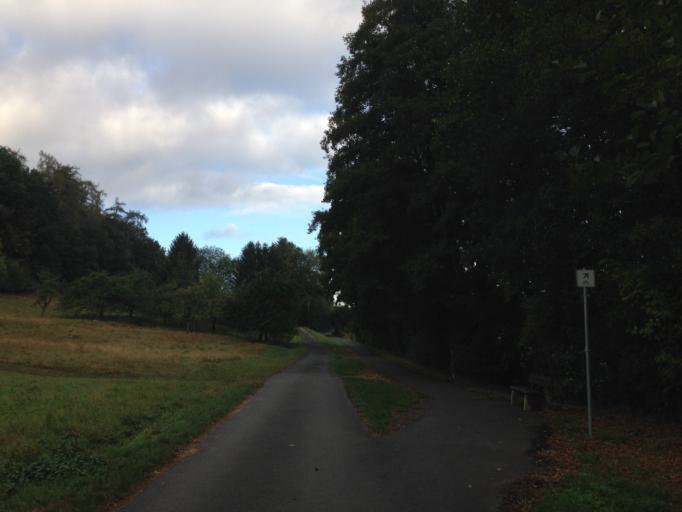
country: DE
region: Hesse
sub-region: Regierungsbezirk Giessen
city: Heuchelheim
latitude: 50.6146
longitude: 8.5999
